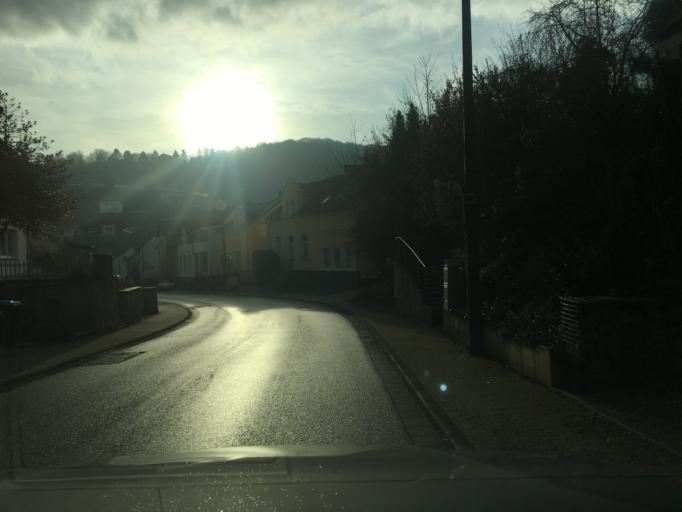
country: DE
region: Rheinland-Pfalz
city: Remagen
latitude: 50.5788
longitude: 7.2226
